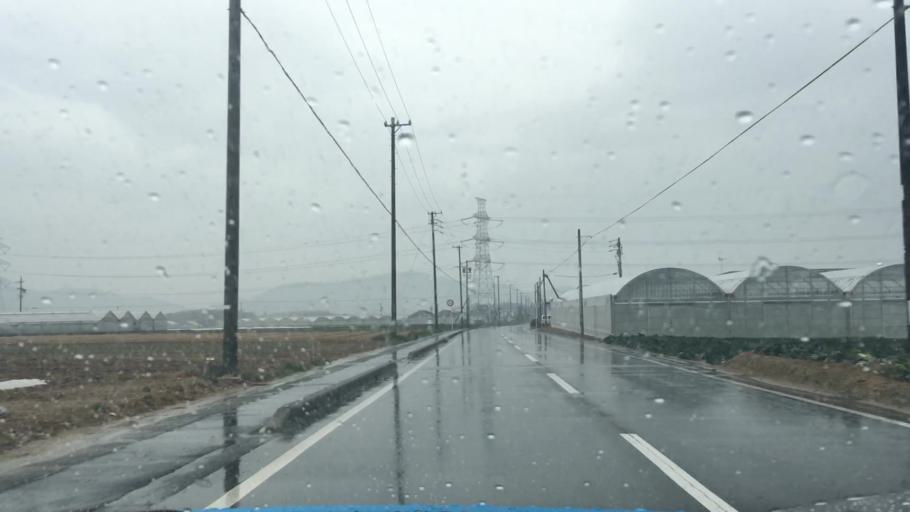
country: JP
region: Aichi
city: Tahara
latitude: 34.6508
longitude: 137.2914
